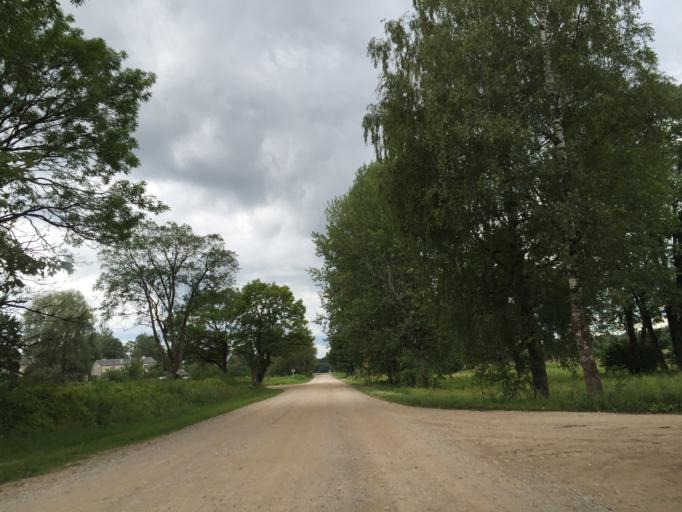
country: LV
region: Malpils
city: Malpils
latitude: 56.8591
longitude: 25.0249
